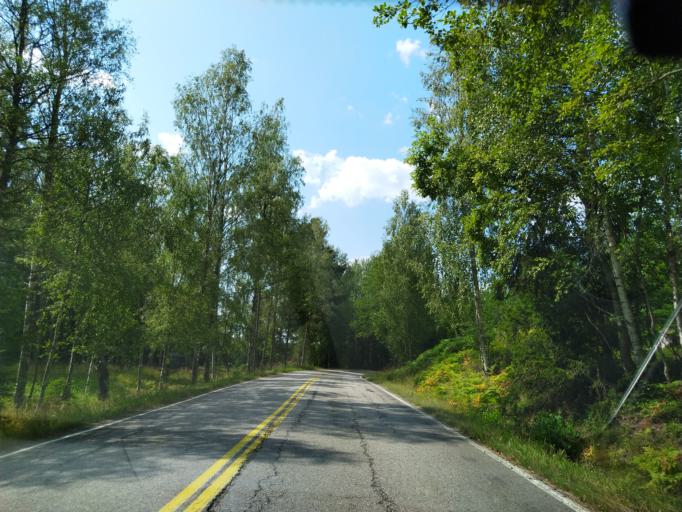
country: FI
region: Uusimaa
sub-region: Helsinki
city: Kirkkonummi
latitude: 60.0155
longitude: 24.4727
